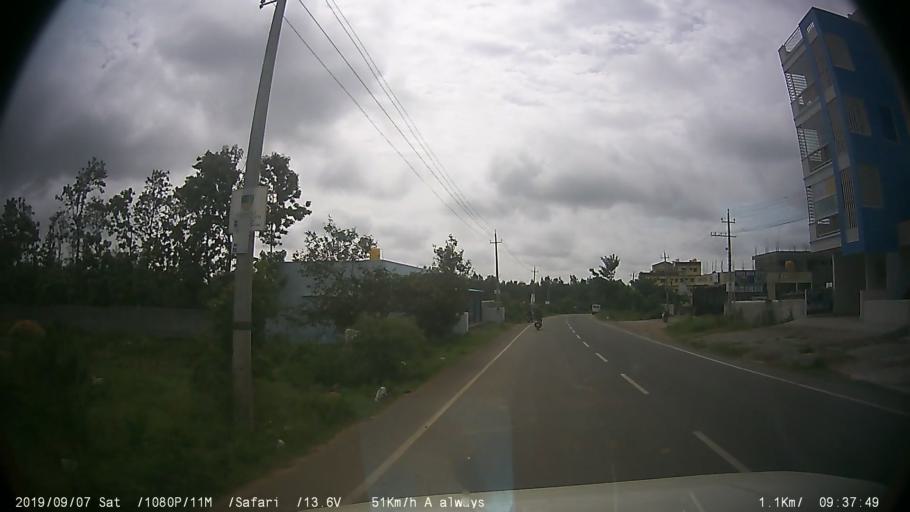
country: IN
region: Karnataka
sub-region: Bangalore Urban
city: Anekal
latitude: 12.8205
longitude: 77.6246
